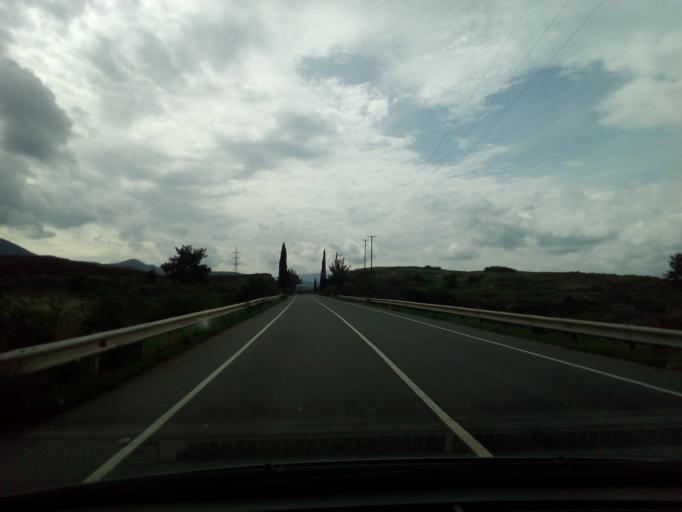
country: CY
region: Lefkosia
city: Lefka
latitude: 35.0826
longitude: 32.9504
